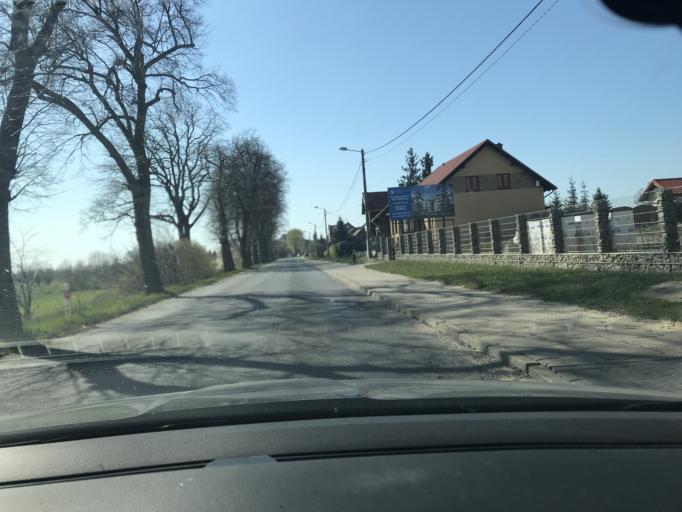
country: PL
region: Pomeranian Voivodeship
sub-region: Powiat nowodworski
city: Sztutowo
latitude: 54.3261
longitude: 19.1717
